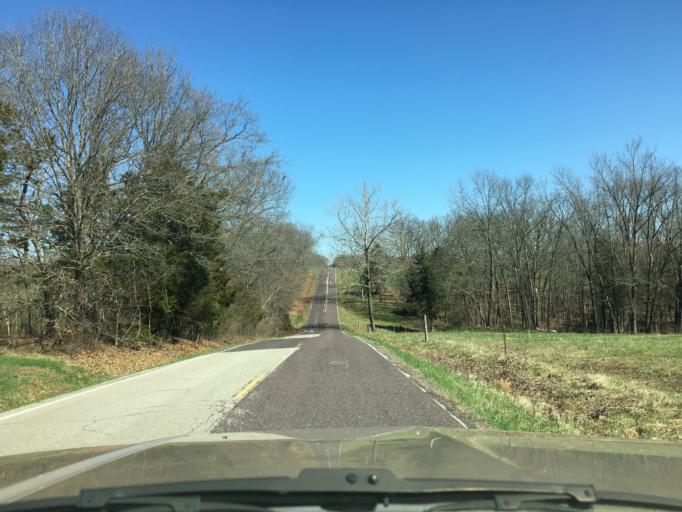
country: US
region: Missouri
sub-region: Franklin County
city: New Haven
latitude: 38.5499
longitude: -91.3303
